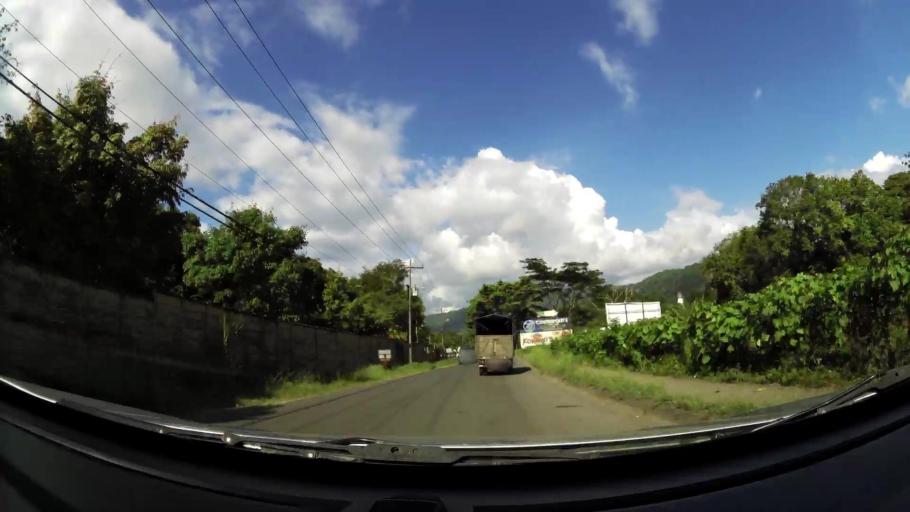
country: CR
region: Puntarenas
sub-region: Canton de Garabito
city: Jaco
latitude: 9.6597
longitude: -84.6412
